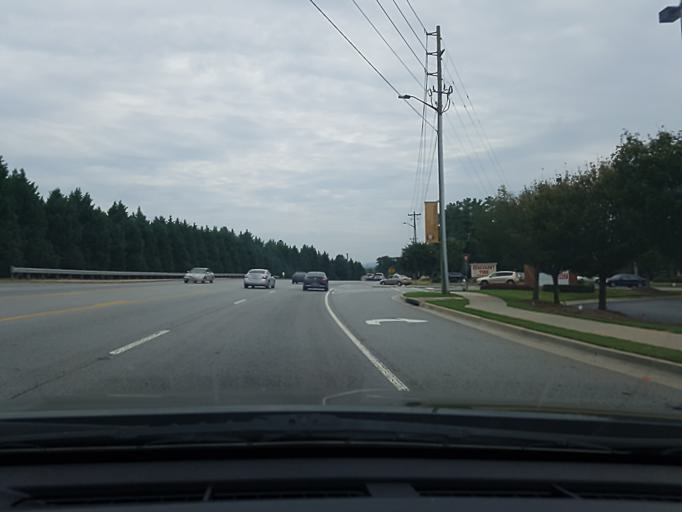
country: US
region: Georgia
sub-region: Gwinnett County
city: Duluth
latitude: 33.9612
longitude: -84.1414
